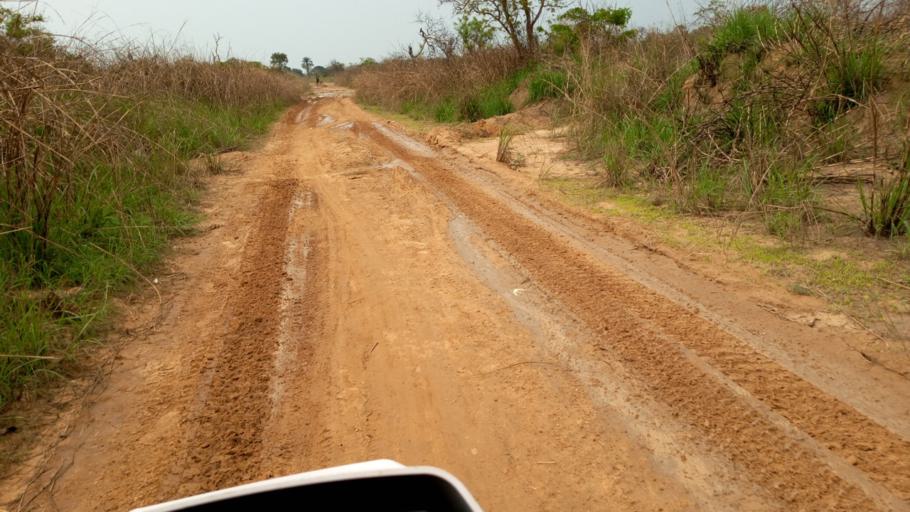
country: CD
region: Bandundu
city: Bandundu
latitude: -3.4811
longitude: 17.7855
